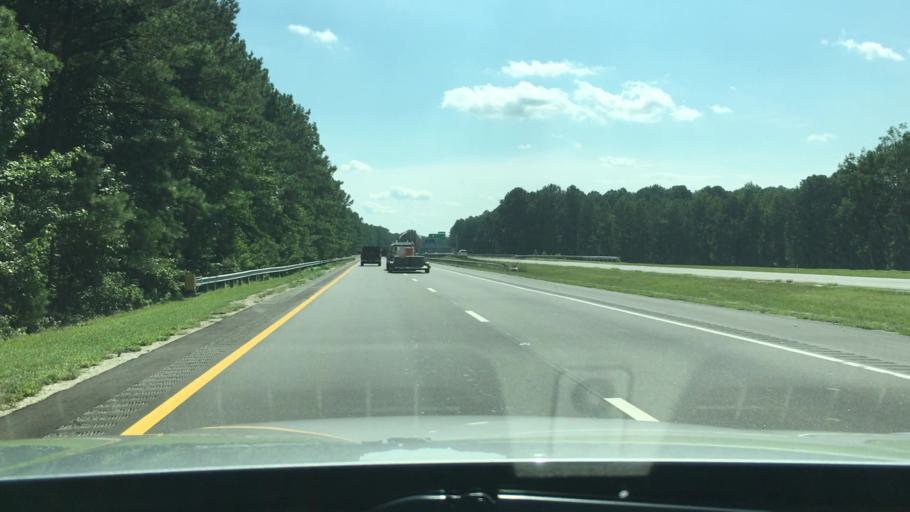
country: US
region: North Carolina
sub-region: Cumberland County
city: Fayetteville
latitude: 34.9785
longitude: -78.8549
